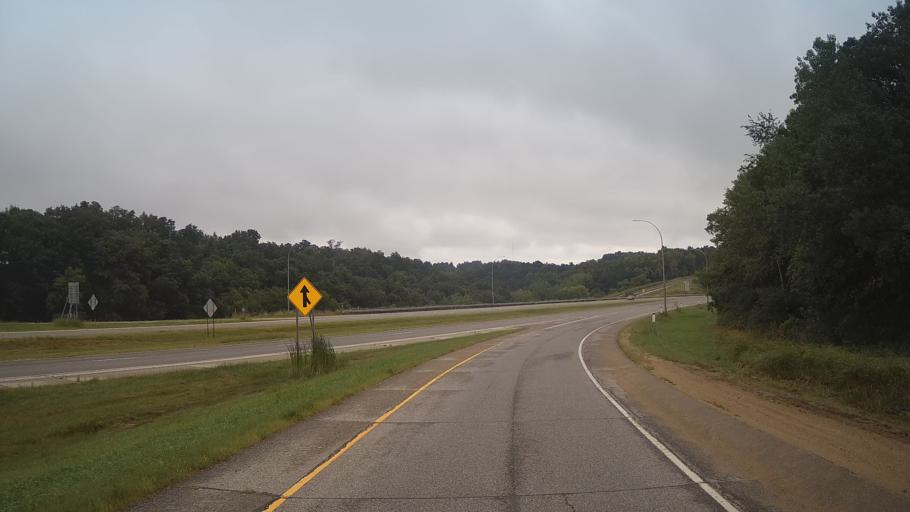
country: US
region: Wisconsin
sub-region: Trempealeau County
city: Trempealeau
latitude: 43.9269
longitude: -91.4364
